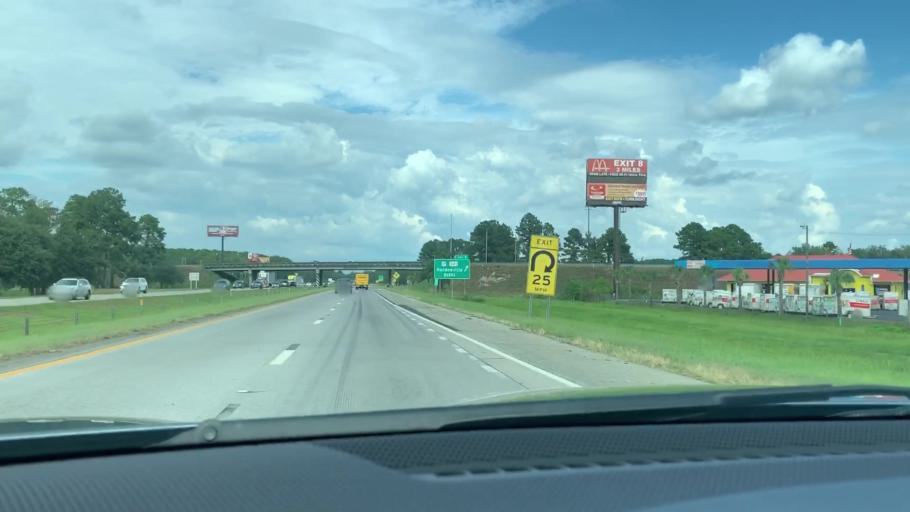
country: US
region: South Carolina
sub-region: Jasper County
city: Hardeeville
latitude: 32.2716
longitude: -81.0822
